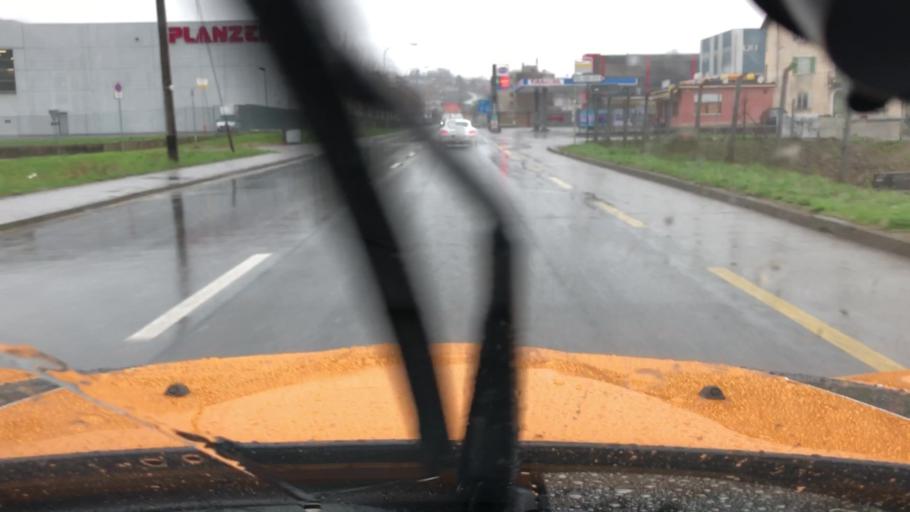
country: CH
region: Ticino
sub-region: Mendrisio District
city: Balerna
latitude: 45.8376
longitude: 9.0064
